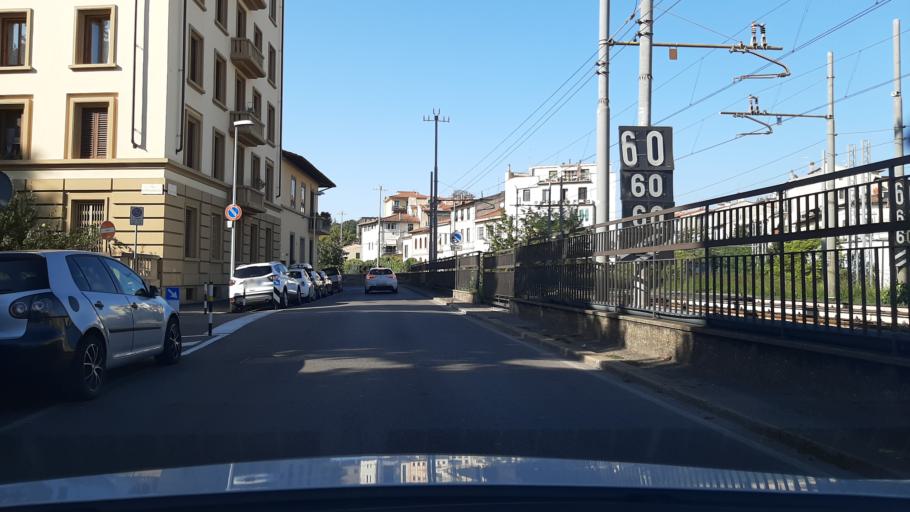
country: IT
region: Tuscany
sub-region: Province of Florence
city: Florence
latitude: 43.7868
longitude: 11.2674
